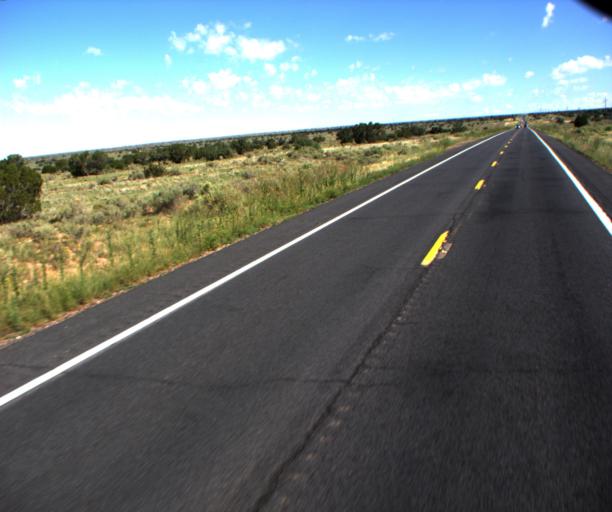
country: US
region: Arizona
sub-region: Coconino County
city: Grand Canyon Village
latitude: 35.7237
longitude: -112.1311
